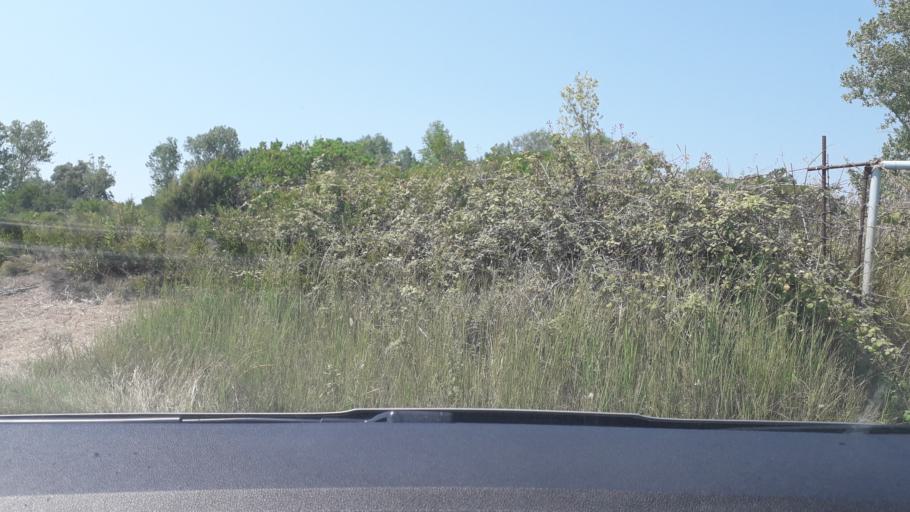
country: GR
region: Ionian Islands
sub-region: Nomos Kerkyras
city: Agios Matthaios
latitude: 39.4551
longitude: 19.8851
